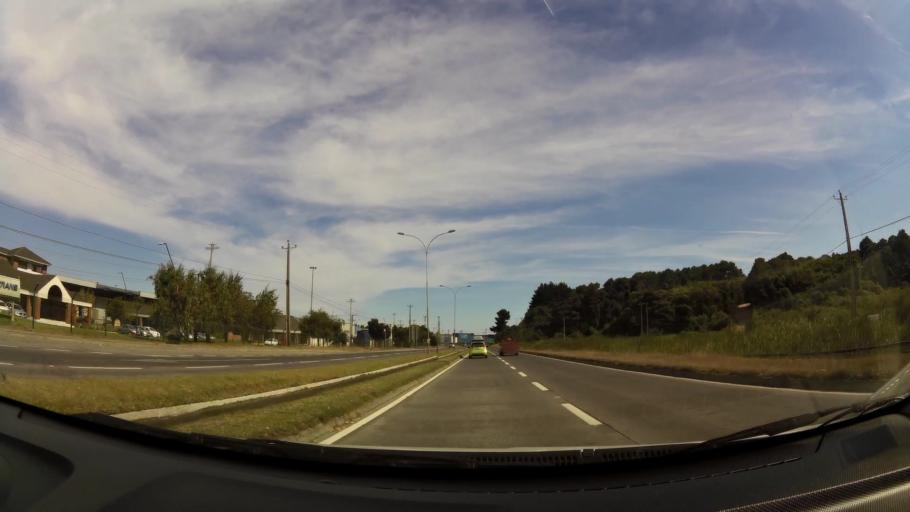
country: CL
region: Biobio
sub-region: Provincia de Concepcion
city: Talcahuano
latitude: -36.7597
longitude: -73.1198
